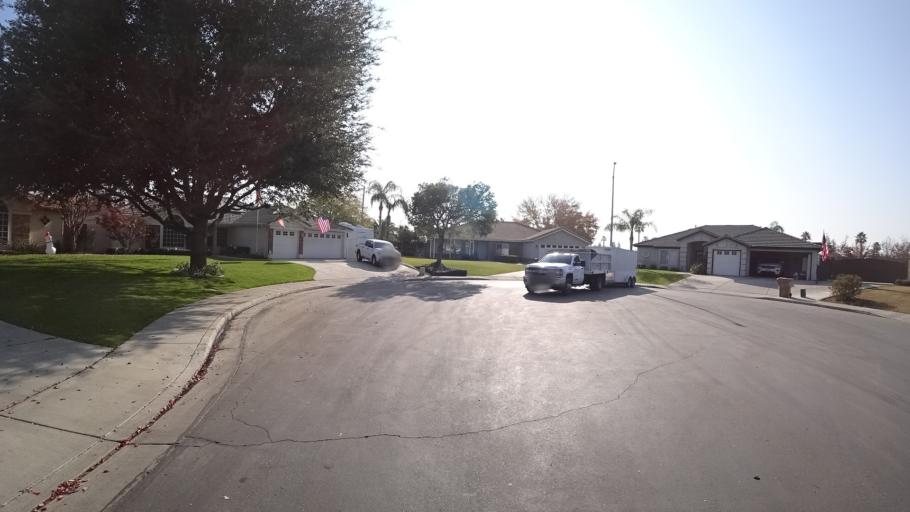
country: US
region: California
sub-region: Kern County
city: Greenacres
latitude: 35.4060
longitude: -119.1109
